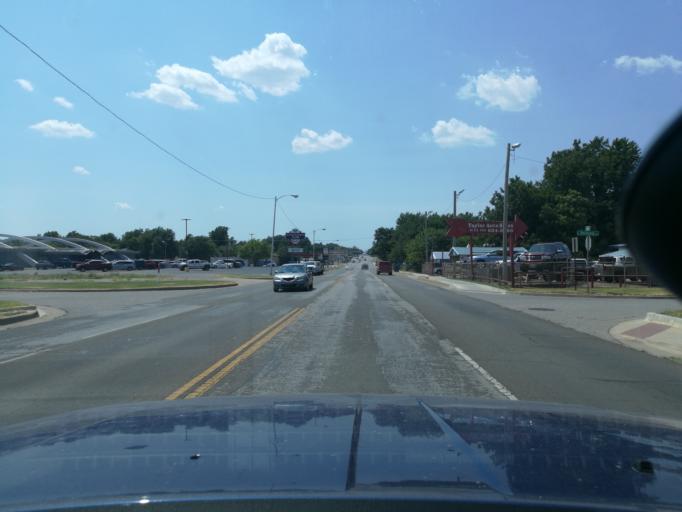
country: US
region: Oklahoma
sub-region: Oklahoma County
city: Oklahoma City
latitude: 35.4207
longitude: -97.5100
